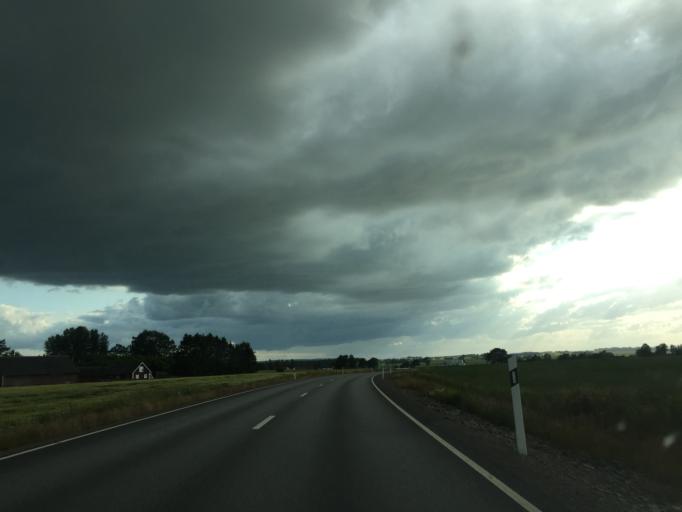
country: SE
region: OEstergoetland
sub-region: Vadstena Kommun
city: Vadstena
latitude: 58.4365
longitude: 14.9136
